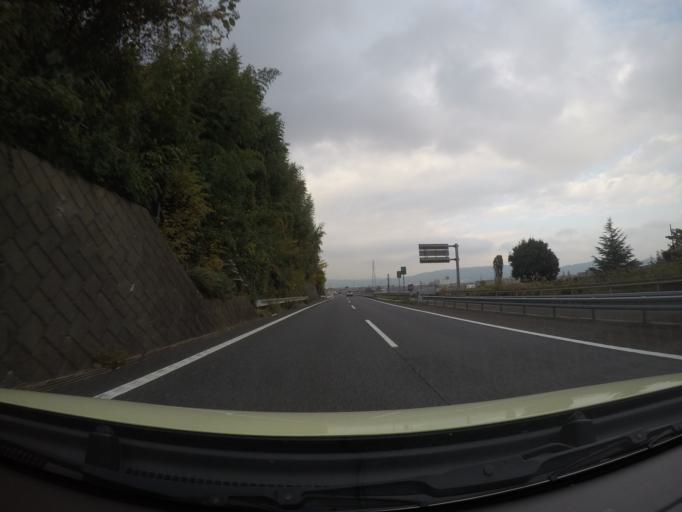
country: JP
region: Kanagawa
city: Odawara
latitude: 35.2759
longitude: 139.1506
